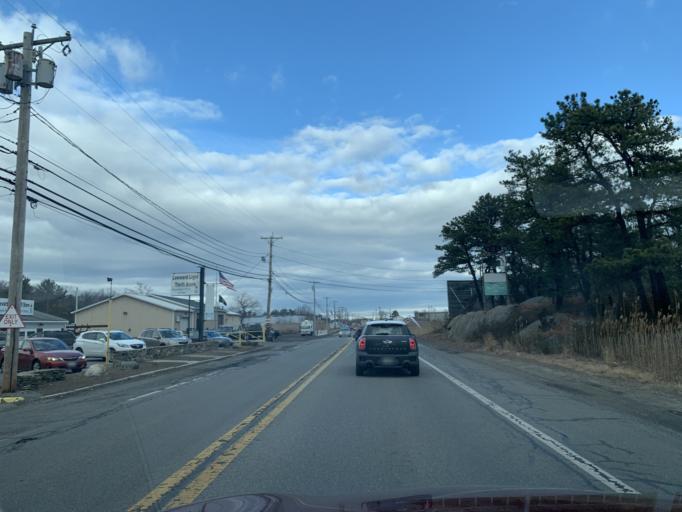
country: US
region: Massachusetts
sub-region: Essex County
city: Newburyport
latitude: 42.8233
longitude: -70.8667
